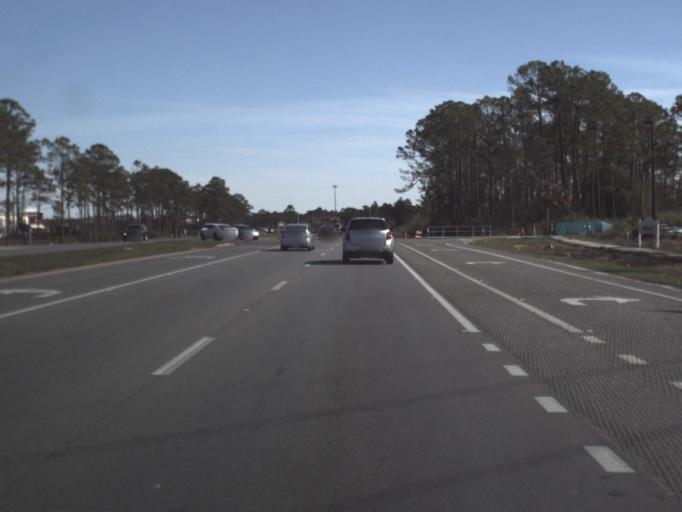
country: US
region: Florida
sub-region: Bay County
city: Panama City Beach
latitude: 30.1991
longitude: -85.8174
